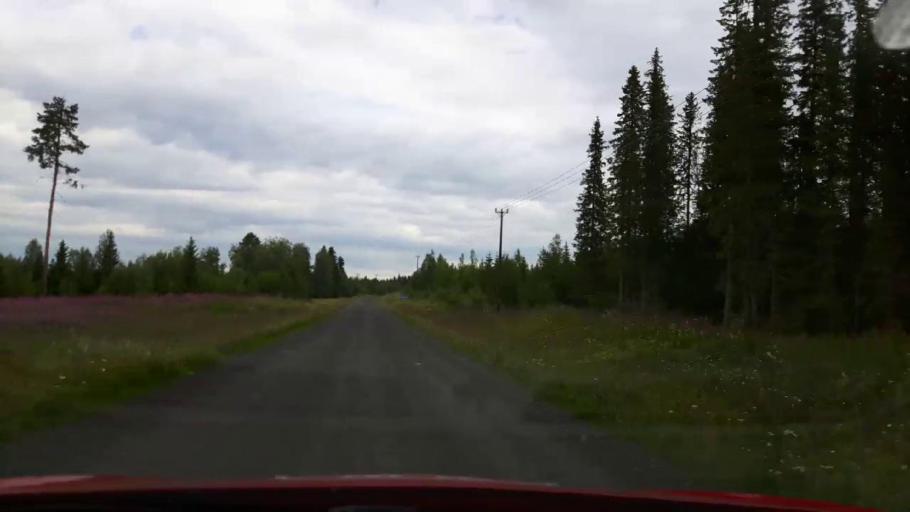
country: SE
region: Jaemtland
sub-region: Stroemsunds Kommun
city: Stroemsund
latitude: 63.4855
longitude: 15.3066
